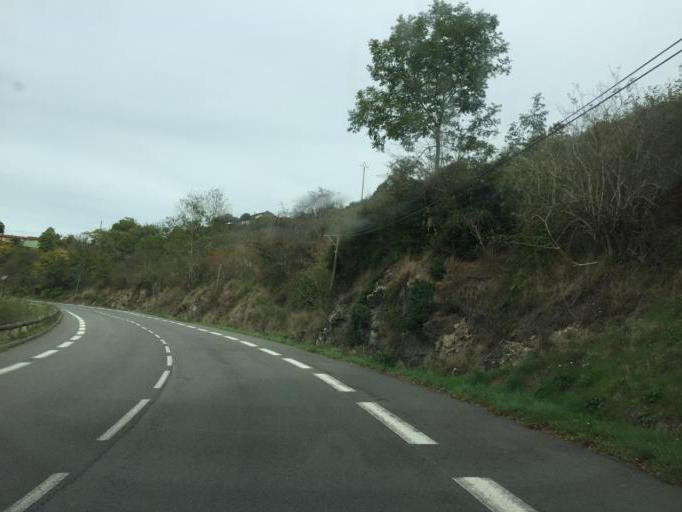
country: FR
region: Rhone-Alpes
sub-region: Departement du Rhone
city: Grandris
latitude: 45.9849
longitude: 4.5098
